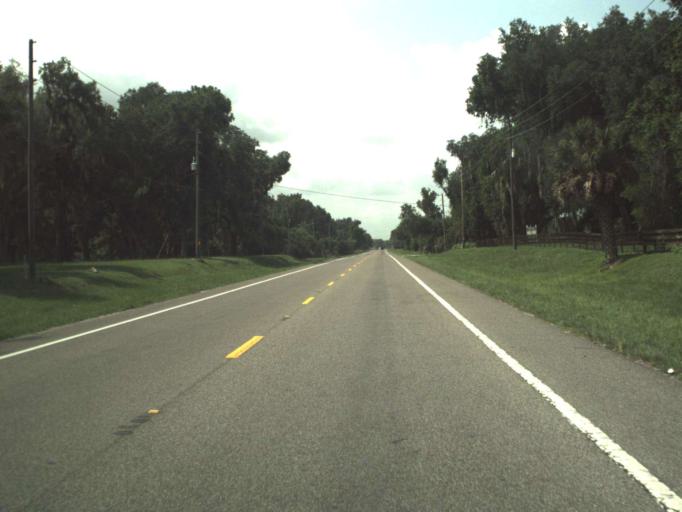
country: US
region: Florida
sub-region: Sumter County
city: Wildwood
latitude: 28.8214
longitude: -82.0456
